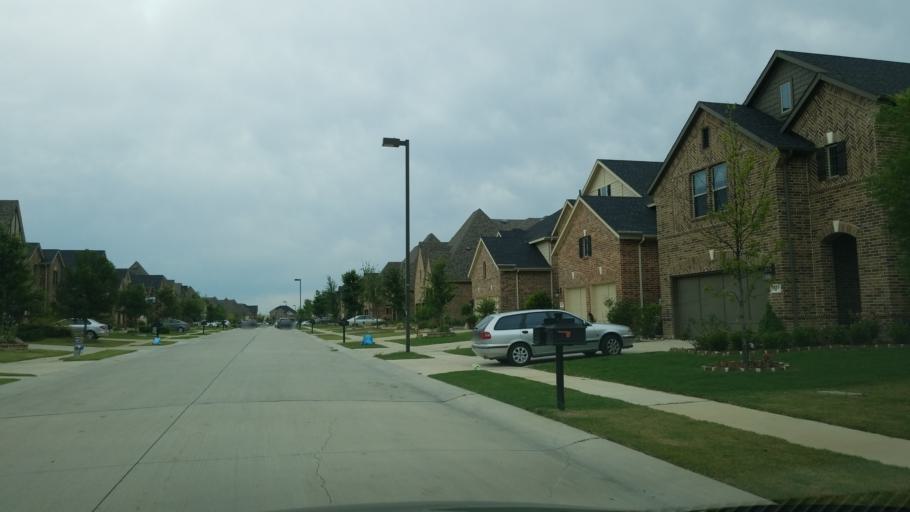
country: US
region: Texas
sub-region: Dallas County
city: Coppell
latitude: 32.8989
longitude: -96.9866
